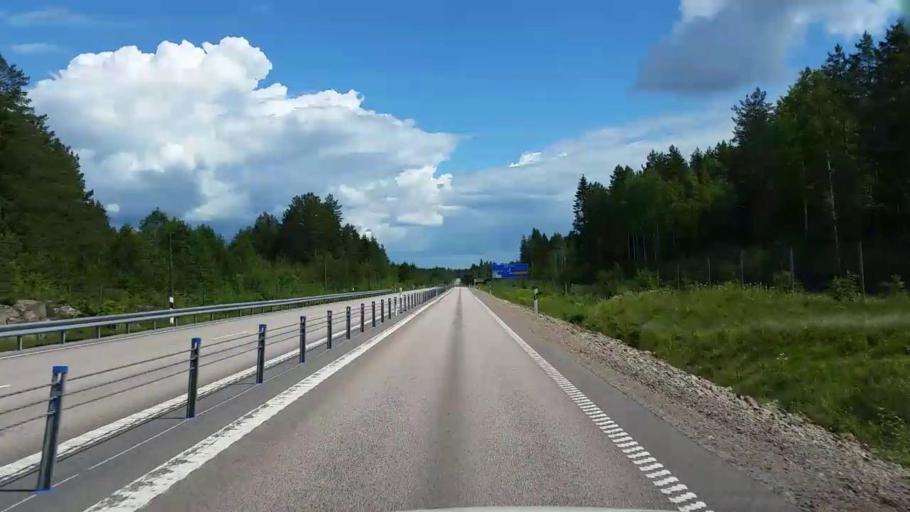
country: SE
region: Dalarna
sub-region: Avesta Kommun
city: Avesta
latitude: 60.1209
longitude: 16.0887
